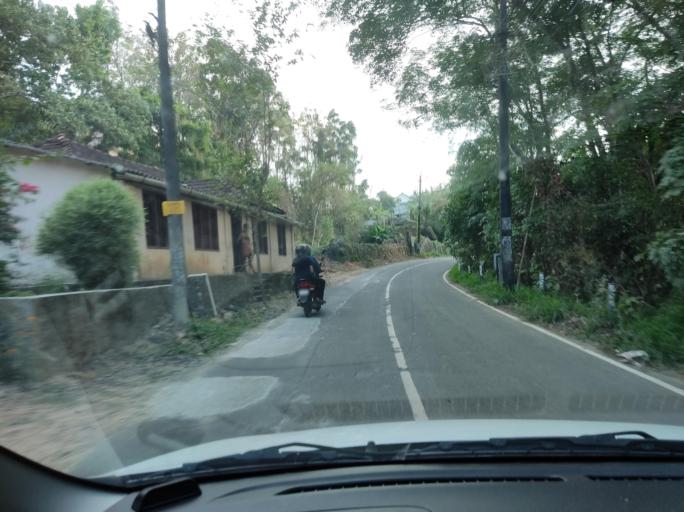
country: IN
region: Kerala
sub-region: Kottayam
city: Kottayam
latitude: 9.6443
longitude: 76.5180
